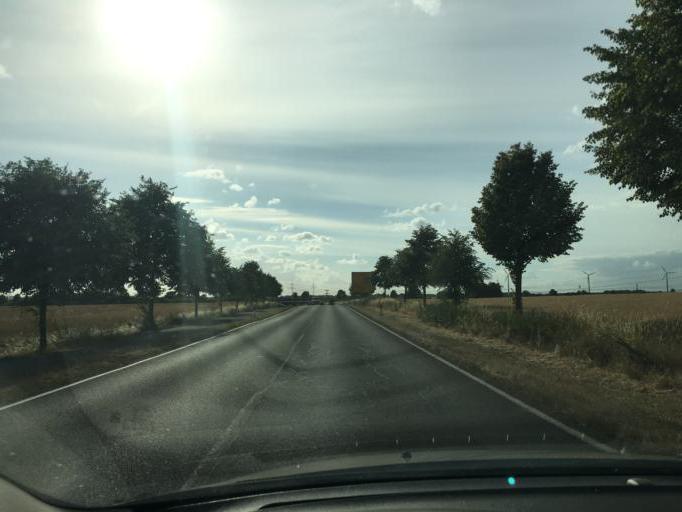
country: DE
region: Saxony-Anhalt
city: Wolmirstedt
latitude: 52.2517
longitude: 11.6104
